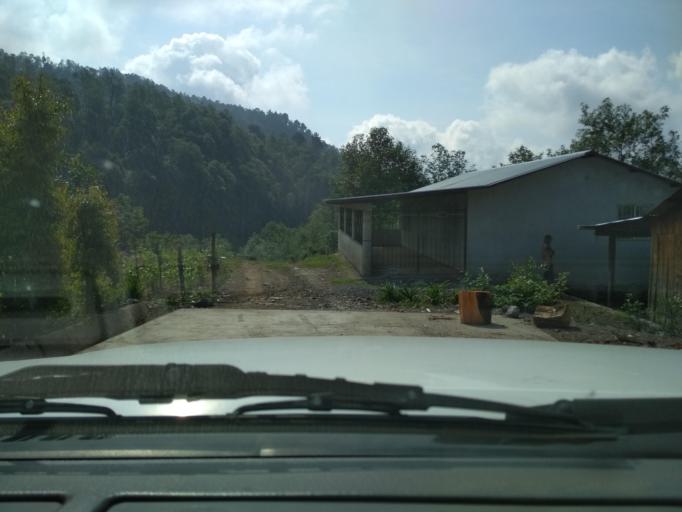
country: MX
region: Veracruz
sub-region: La Perla
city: Chilapa
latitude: 18.9944
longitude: -97.1777
